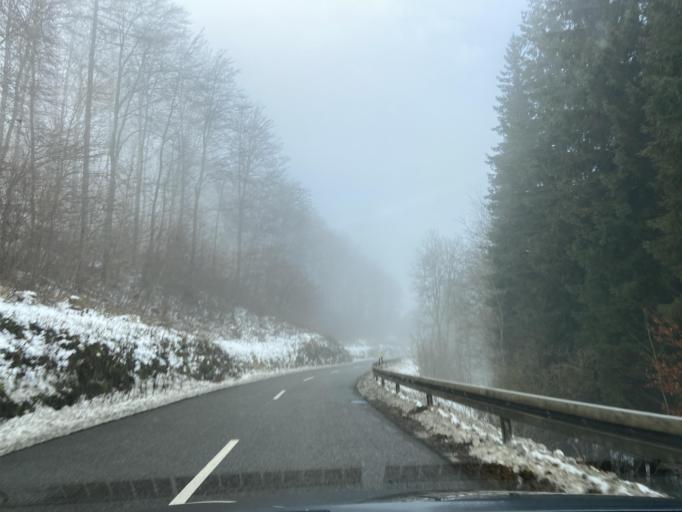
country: DE
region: Baden-Wuerttemberg
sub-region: Tuebingen Region
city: Hettingen
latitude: 48.2145
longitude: 9.2396
